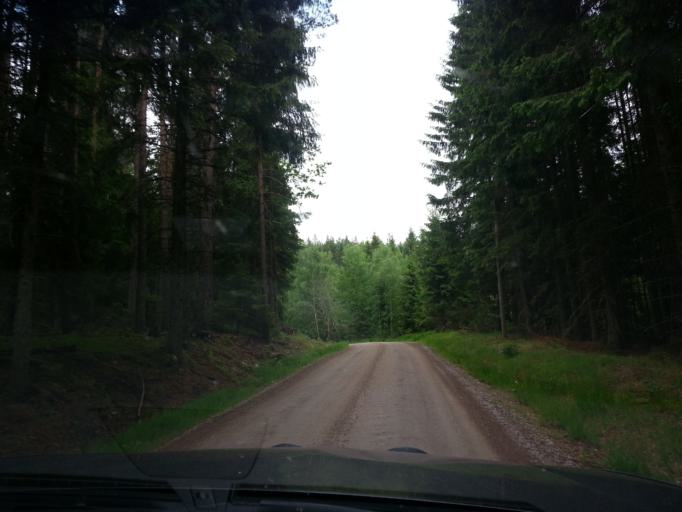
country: SE
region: Joenkoeping
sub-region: Vetlanda Kommun
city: Vetlanda
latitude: 57.2844
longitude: 15.1355
